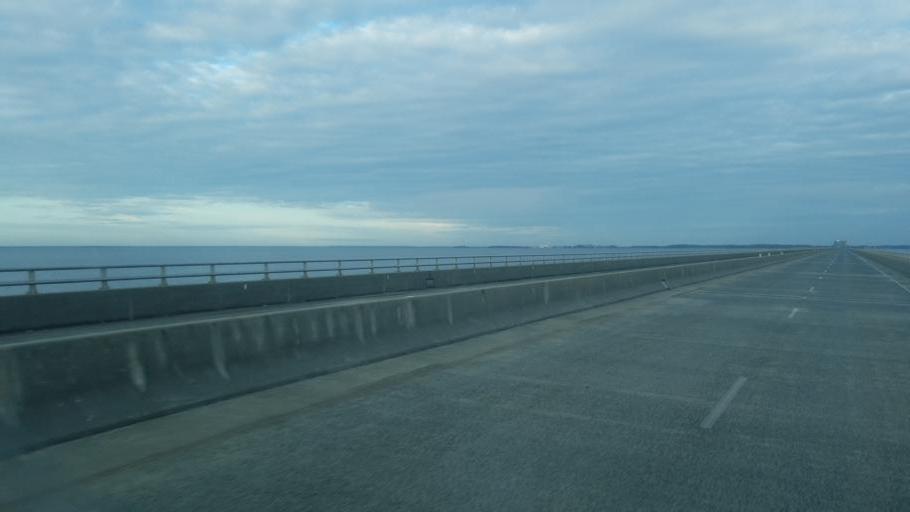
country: US
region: North Carolina
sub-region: Dare County
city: Manteo
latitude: 35.8834
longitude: -75.6960
